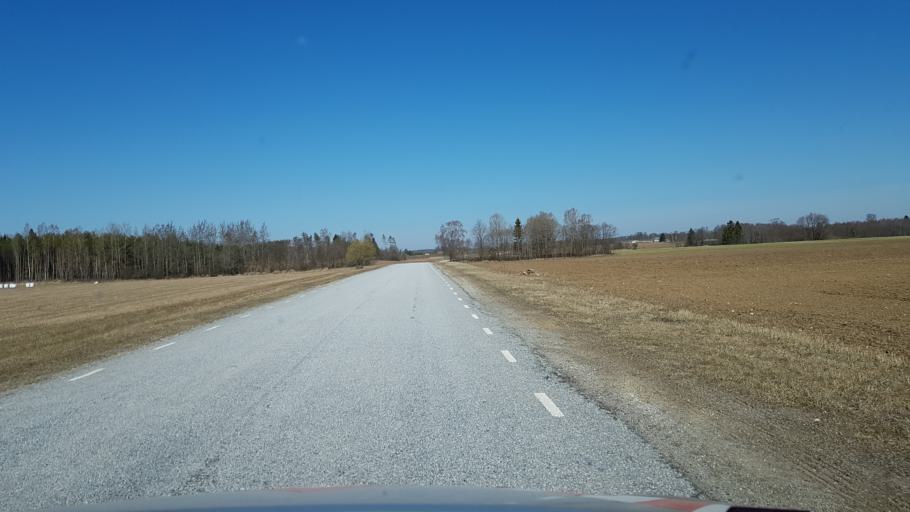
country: EE
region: Jaervamaa
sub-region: Koeru vald
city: Koeru
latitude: 59.0207
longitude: 26.0882
